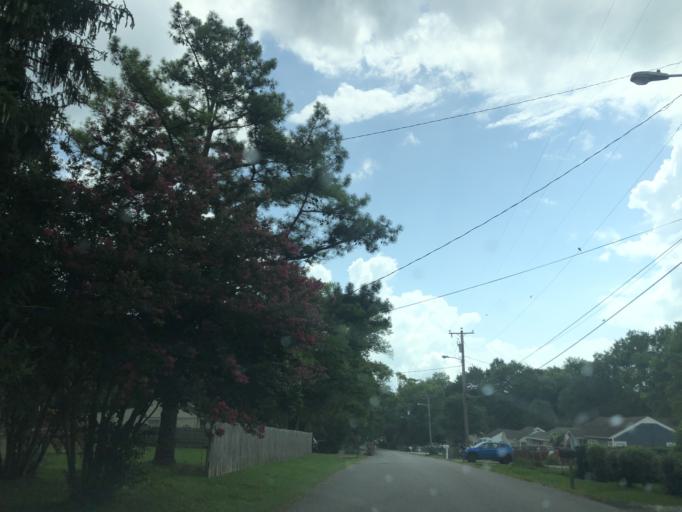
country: US
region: Tennessee
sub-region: Davidson County
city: Lakewood
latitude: 36.1583
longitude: -86.6624
